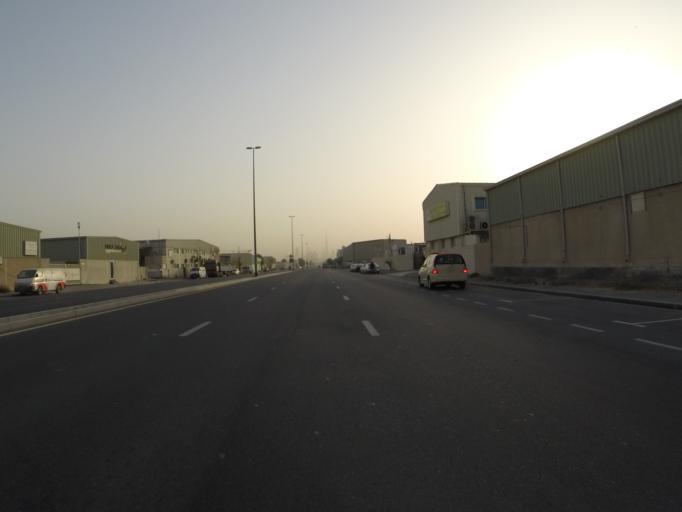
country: AE
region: Dubai
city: Dubai
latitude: 25.1248
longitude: 55.2139
